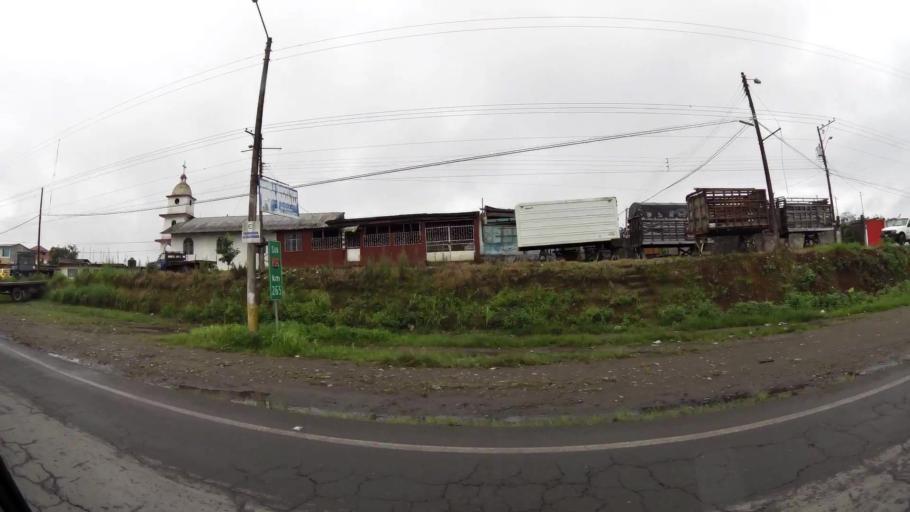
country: EC
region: Santo Domingo de los Tsachilas
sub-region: Canton Santo Domingo de los Colorados
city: Santo Domingo de los Colorados
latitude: -0.2722
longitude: -79.1998
